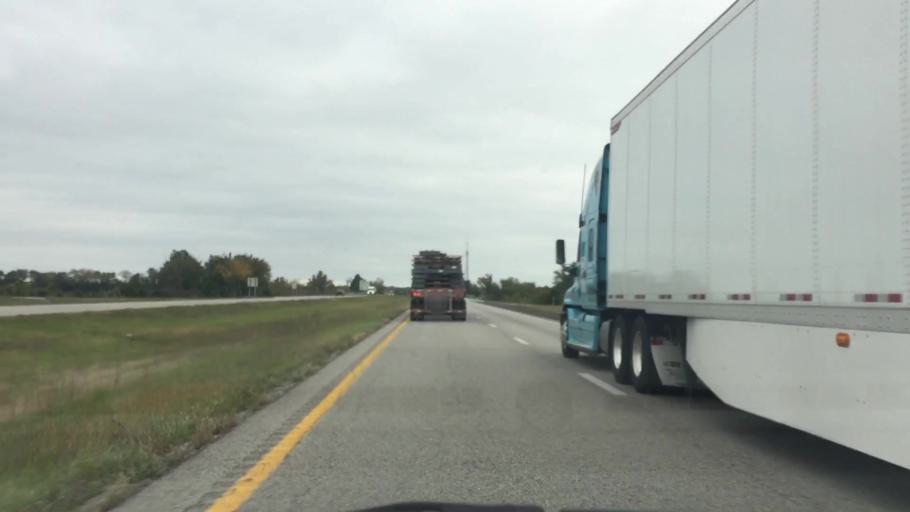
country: US
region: Missouri
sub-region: Clinton County
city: Cameron
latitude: 39.8548
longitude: -94.1761
